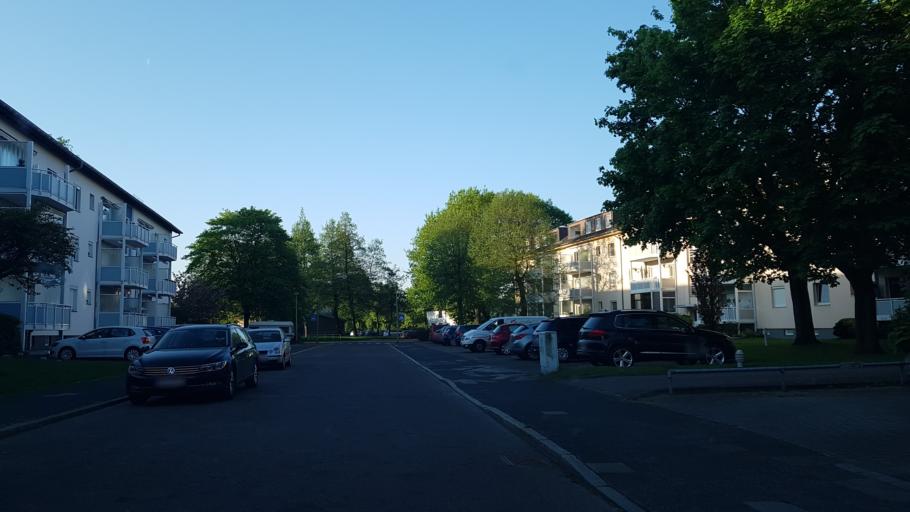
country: DE
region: Lower Saxony
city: Langen
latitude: 53.5753
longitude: 8.5939
